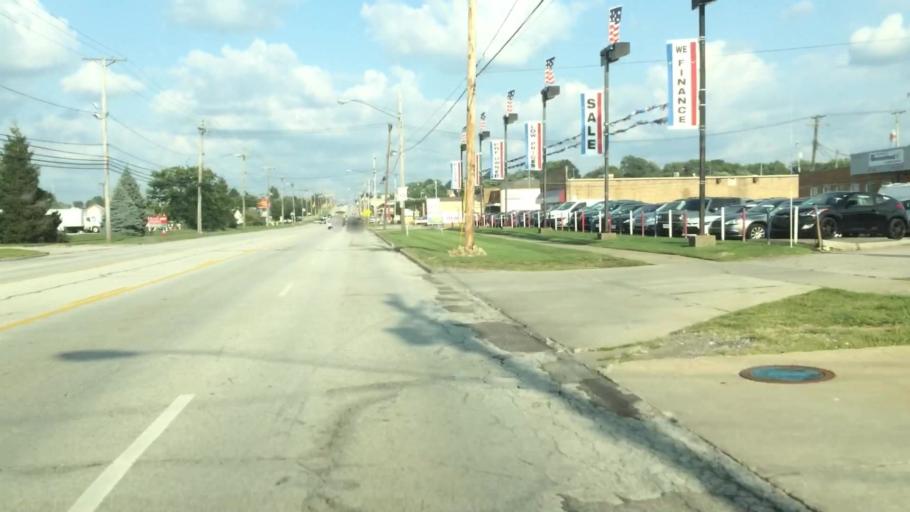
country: US
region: Ohio
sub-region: Cuyahoga County
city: Brooklyn
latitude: 41.4185
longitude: -81.7507
